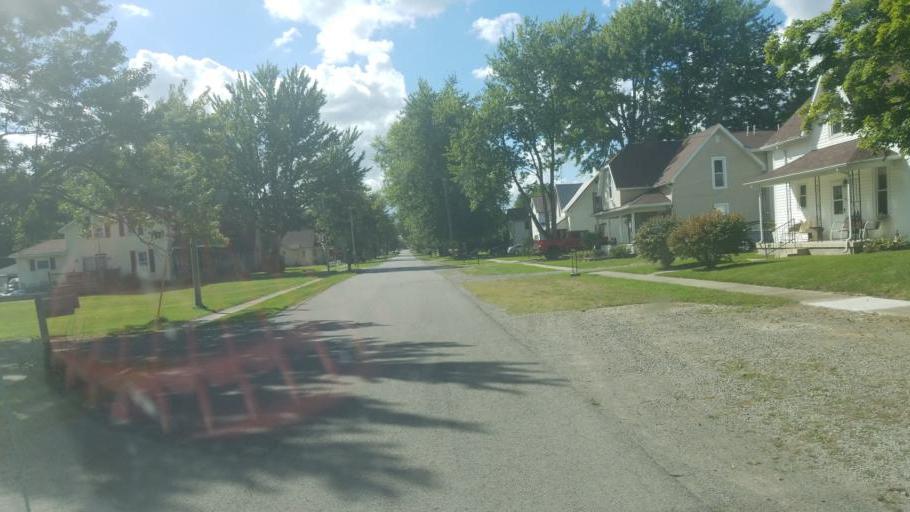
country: US
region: Ohio
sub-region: Hardin County
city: Kenton
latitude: 40.5160
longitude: -83.5648
